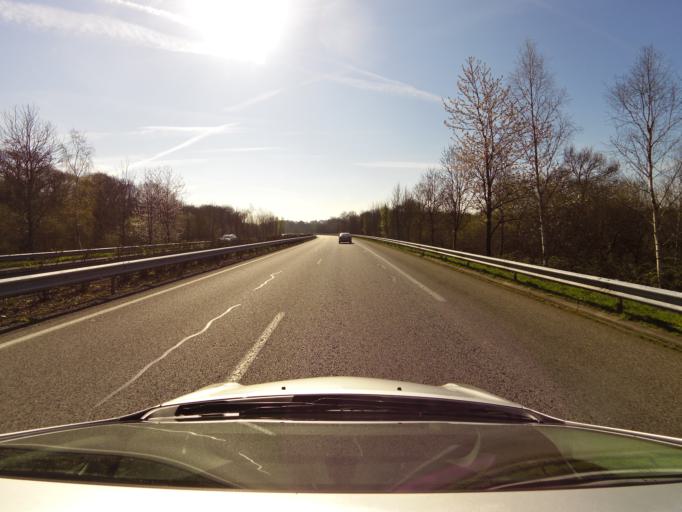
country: FR
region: Brittany
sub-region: Departement du Morbihan
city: Augan
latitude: 47.9266
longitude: -2.2410
